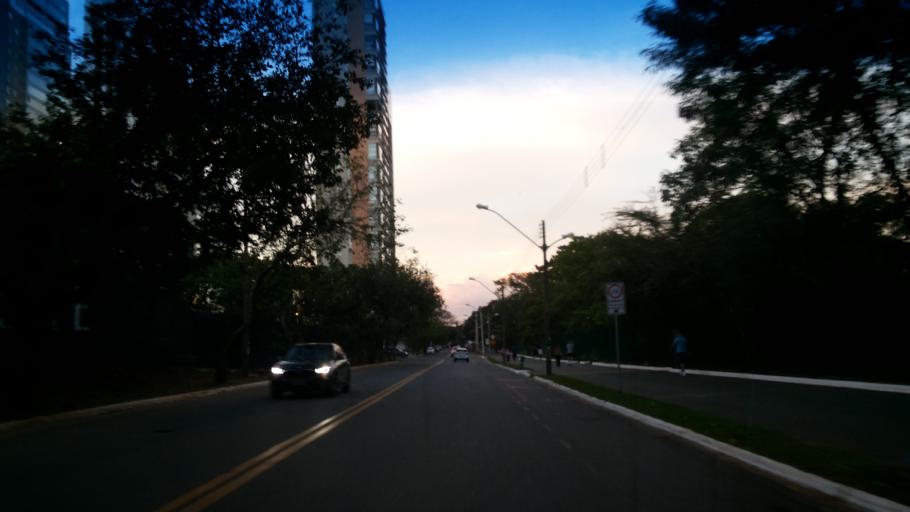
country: BR
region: Goias
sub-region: Goiania
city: Goiania
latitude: -16.7057
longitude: -49.2564
